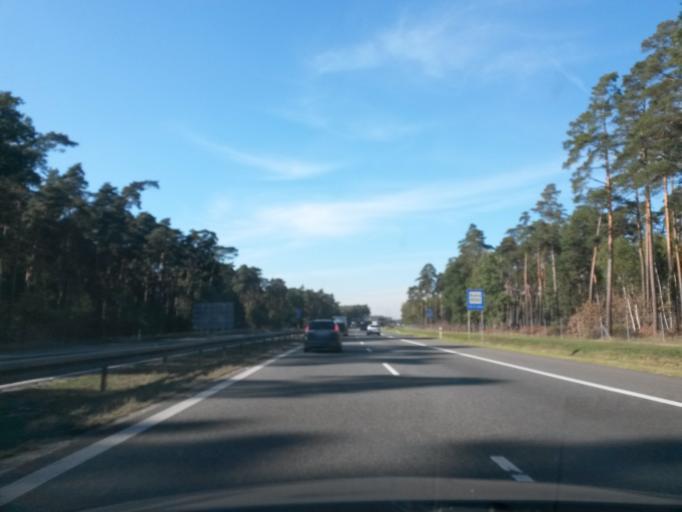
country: PL
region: Opole Voivodeship
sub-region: Powiat opolski
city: Proszkow
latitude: 50.5357
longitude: 17.9053
